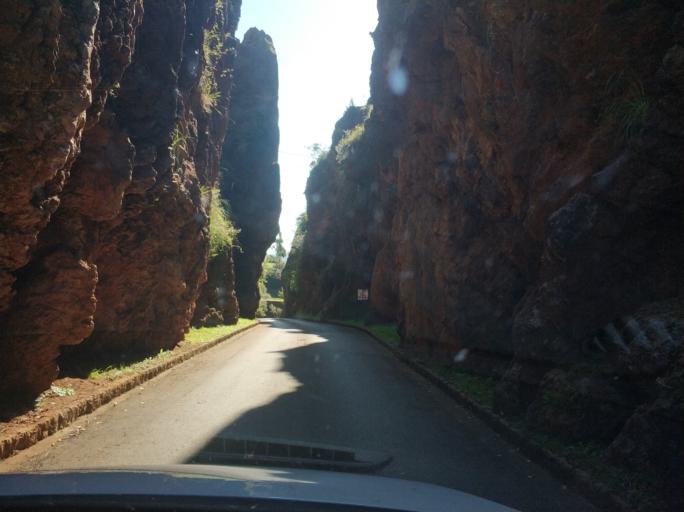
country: ES
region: Cantabria
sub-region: Provincia de Cantabria
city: Penagos
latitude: 43.3549
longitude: -3.8405
